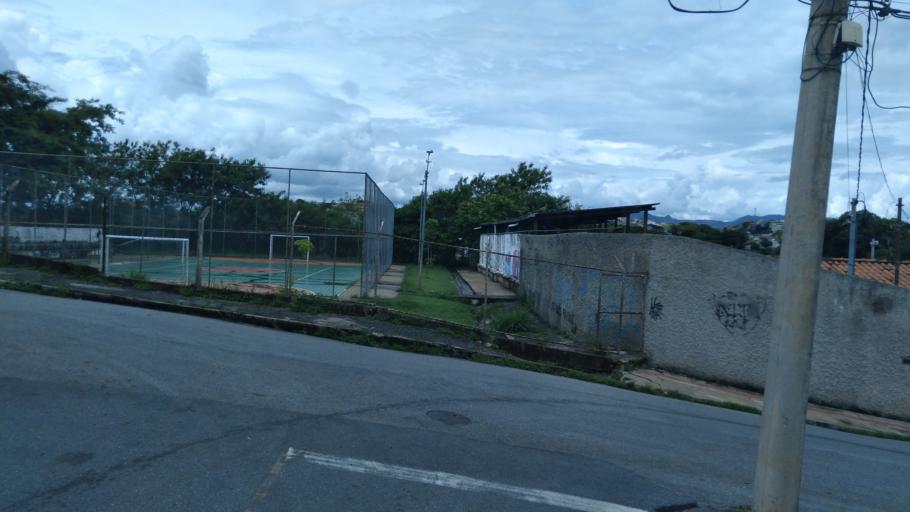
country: BR
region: Minas Gerais
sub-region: Belo Horizonte
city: Belo Horizonte
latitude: -19.8571
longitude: -43.9168
